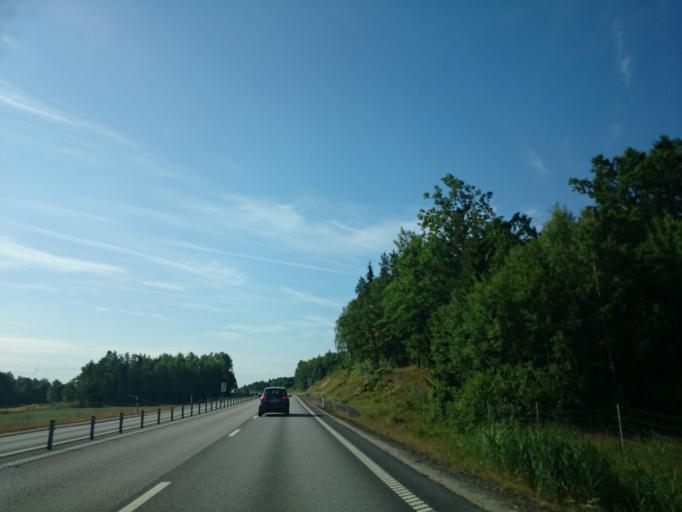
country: SE
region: OEstergoetland
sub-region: Valdemarsviks Kommun
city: Gusum
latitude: 58.3739
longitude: 16.4253
